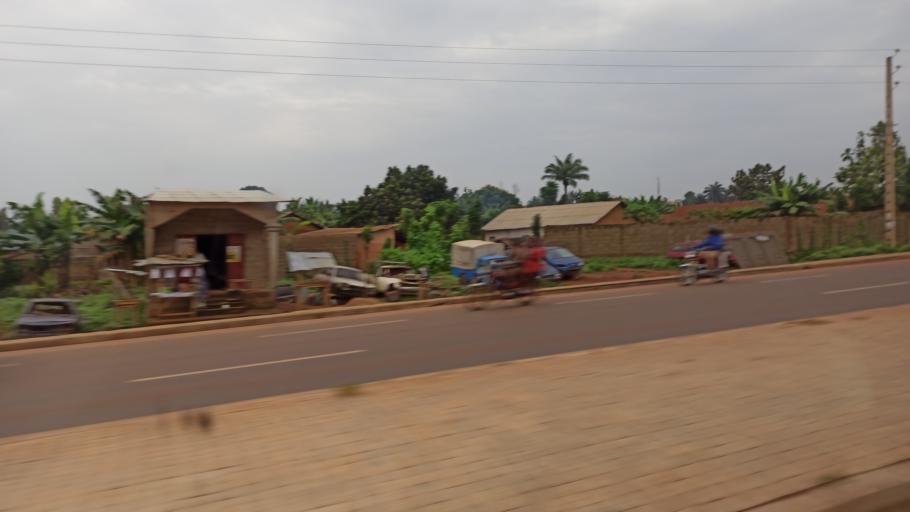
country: BJ
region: Queme
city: Porto-Novo
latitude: 6.5340
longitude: 2.5976
